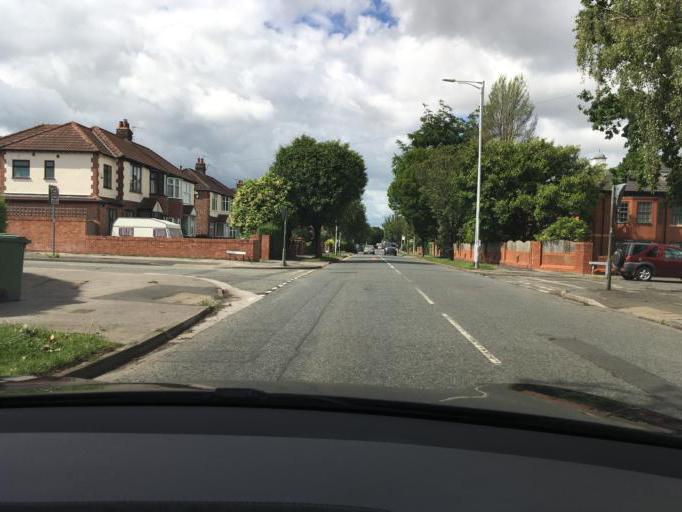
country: GB
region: England
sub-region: Borough of Stockport
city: Stockport
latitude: 53.3907
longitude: -2.1633
